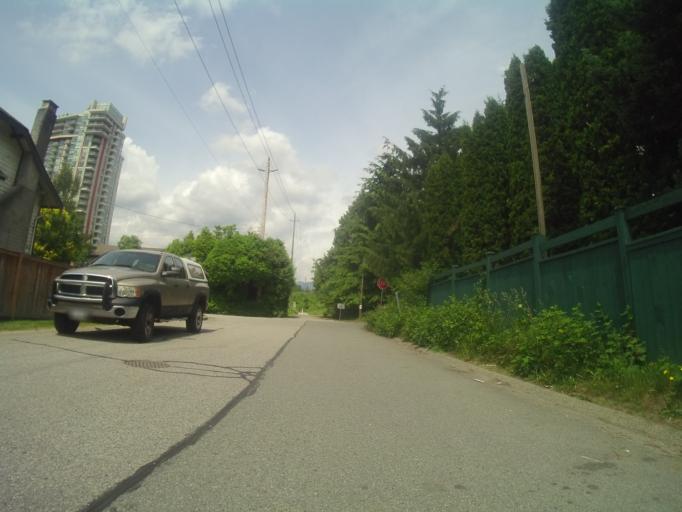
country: CA
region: British Columbia
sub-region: Fraser Valley Regional District
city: North Vancouver
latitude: 49.3103
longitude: -123.0294
